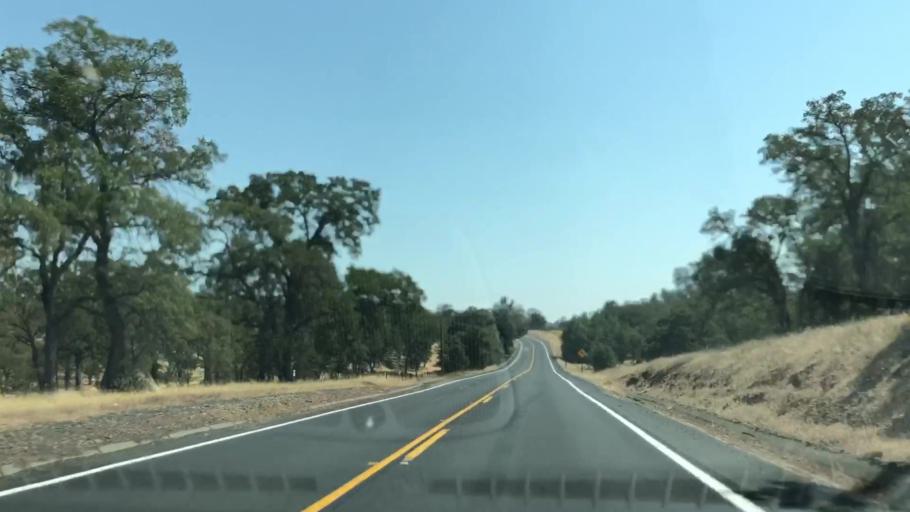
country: US
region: California
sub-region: Calaveras County
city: Copperopolis
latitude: 37.8954
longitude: -120.5536
